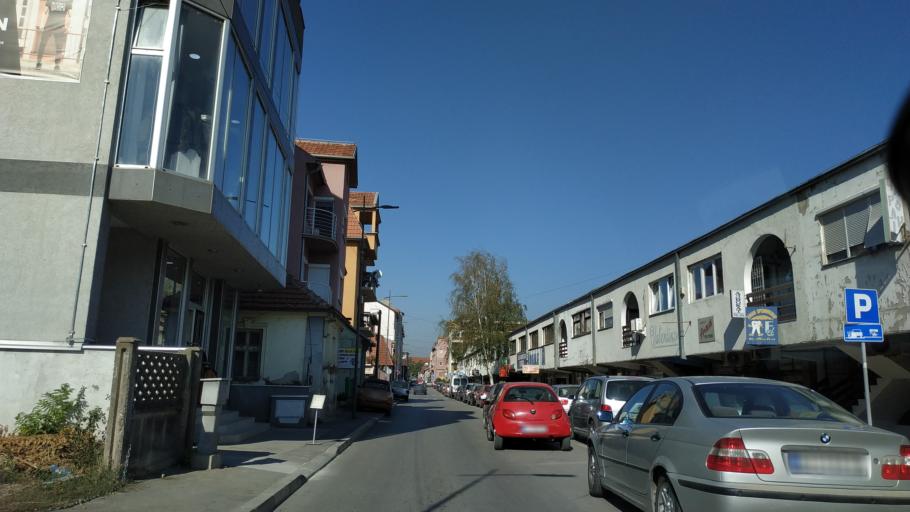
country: RS
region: Central Serbia
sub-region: Nisavski Okrug
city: Aleksinac
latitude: 43.5377
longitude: 21.7110
